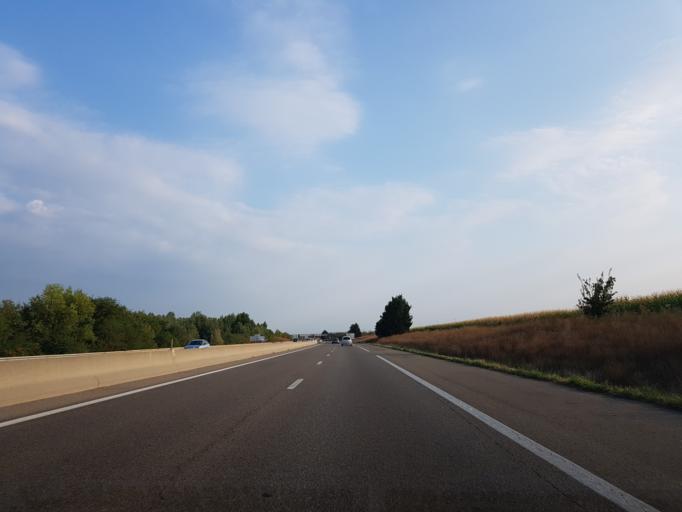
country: FR
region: Alsace
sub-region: Departement du Haut-Rhin
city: Baldersheim
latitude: 47.8076
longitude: 7.3924
